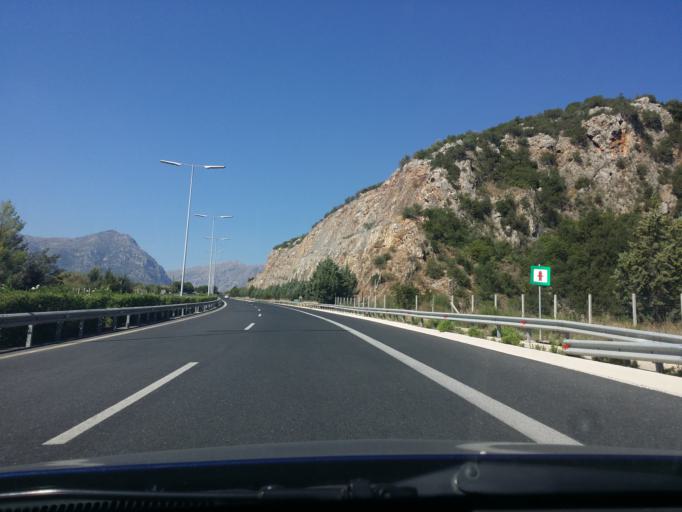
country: GR
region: Peloponnese
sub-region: Nomos Korinthias
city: Nemea
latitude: 37.7176
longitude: 22.5771
